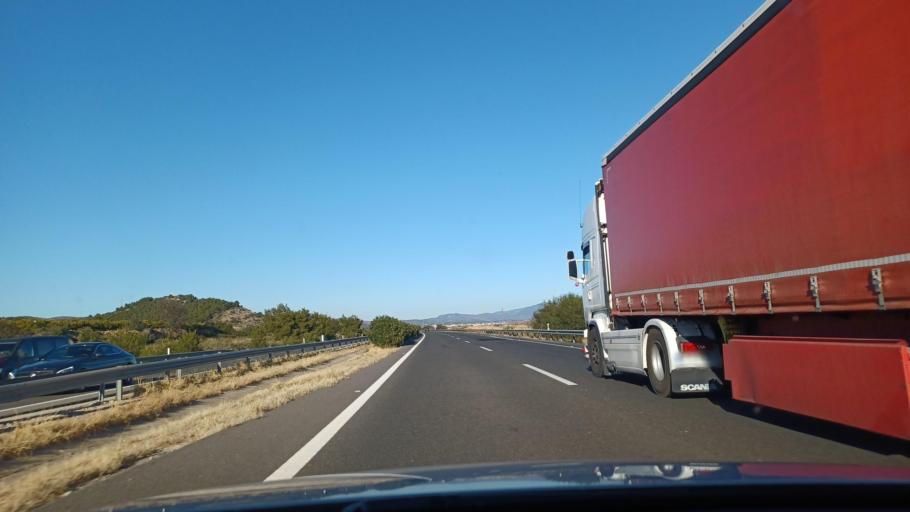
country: ES
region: Valencia
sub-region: Provincia de Castello
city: Orpesa/Oropesa del Mar
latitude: 40.1624
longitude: 0.1568
